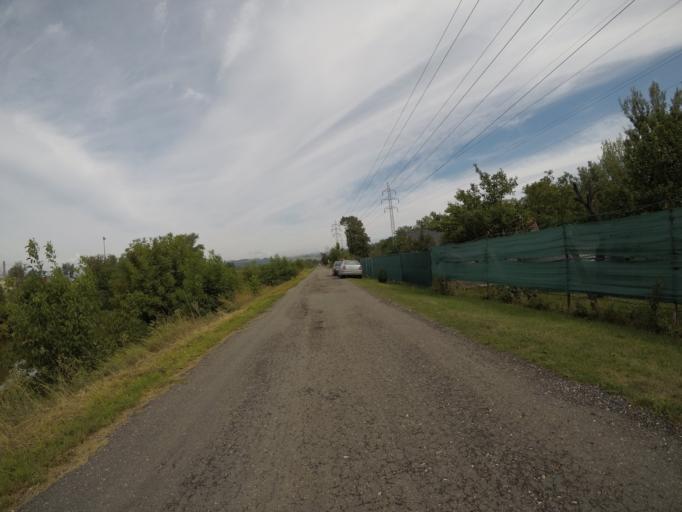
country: SK
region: Trenciansky
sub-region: Okres Nove Mesto nad Vahom
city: Nove Mesto nad Vahom
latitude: 48.7555
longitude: 17.8470
